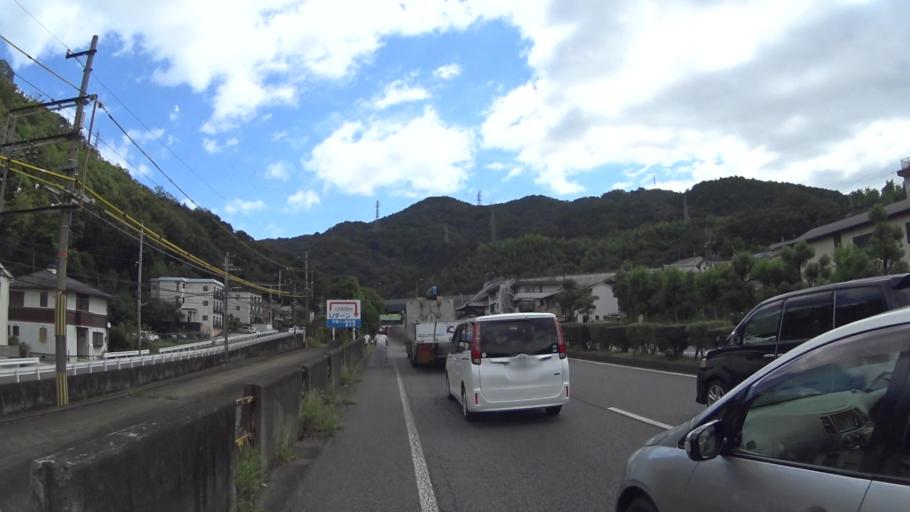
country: JP
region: Shiga Prefecture
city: Otsu-shi
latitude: 34.9911
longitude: 135.8379
